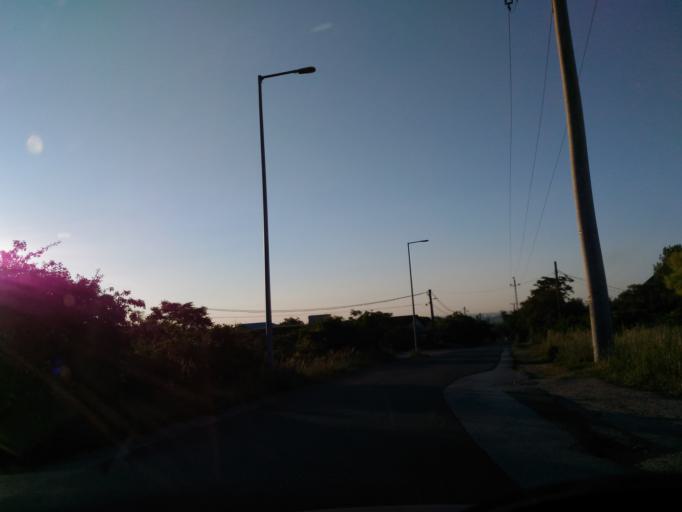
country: HU
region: Pest
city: Diosd
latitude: 47.4164
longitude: 18.9450
